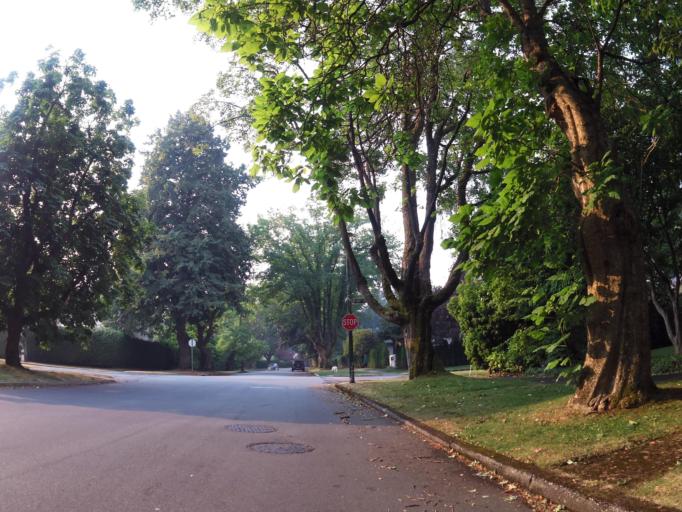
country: CA
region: British Columbia
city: Vancouver
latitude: 49.2402
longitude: -123.1457
